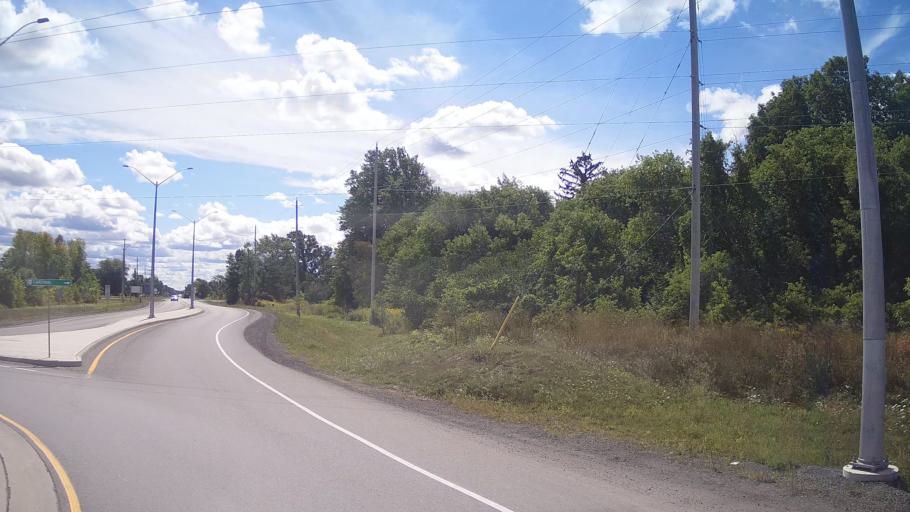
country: US
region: New York
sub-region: St. Lawrence County
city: Ogdensburg
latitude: 44.8468
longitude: -75.3226
